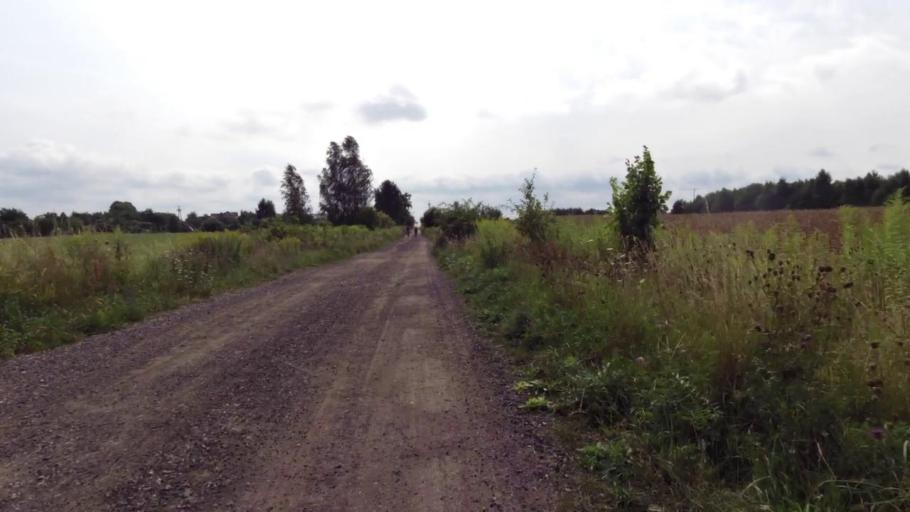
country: PL
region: West Pomeranian Voivodeship
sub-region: Powiat drawski
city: Czaplinek
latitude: 53.5690
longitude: 16.2408
